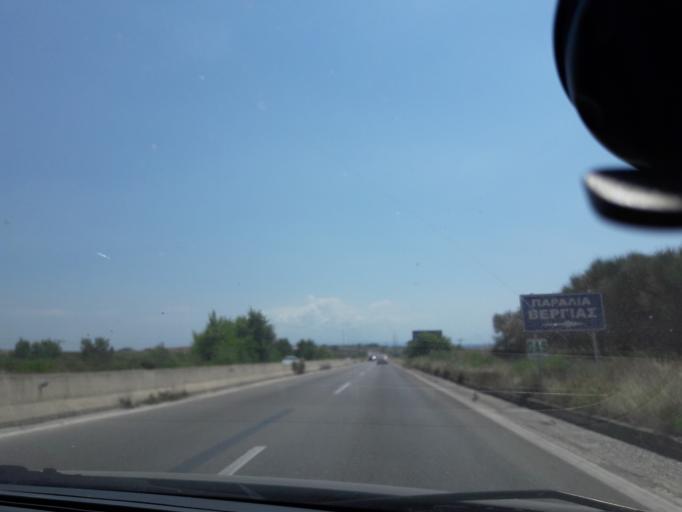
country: GR
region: Central Macedonia
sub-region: Nomos Chalkidikis
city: Nea Triglia
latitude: 40.2924
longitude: 23.1429
